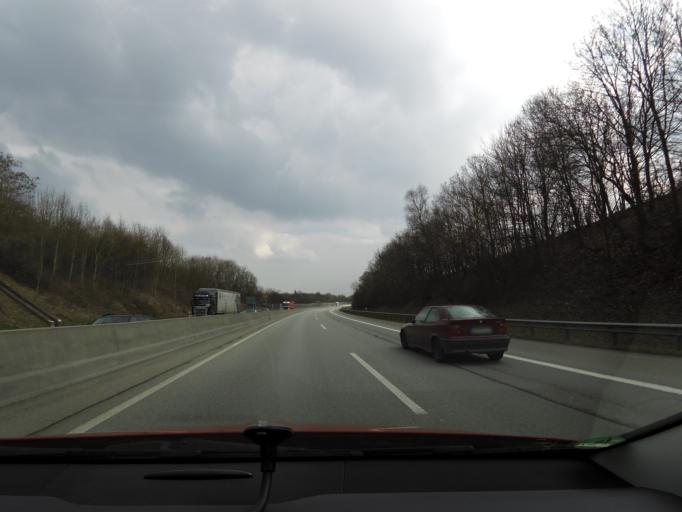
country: DE
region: Rheinland-Pfalz
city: Warmsroth
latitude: 49.9563
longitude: 7.7818
